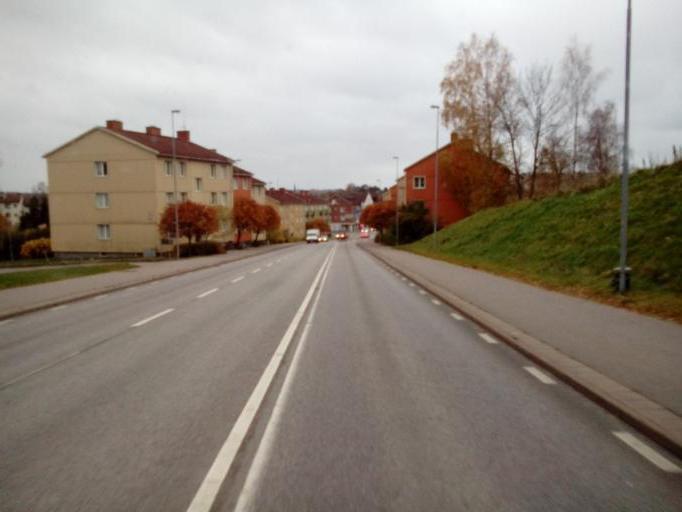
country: SE
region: OErebro
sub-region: Degerfors Kommun
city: Degerfors
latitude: 59.2397
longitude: 14.4342
